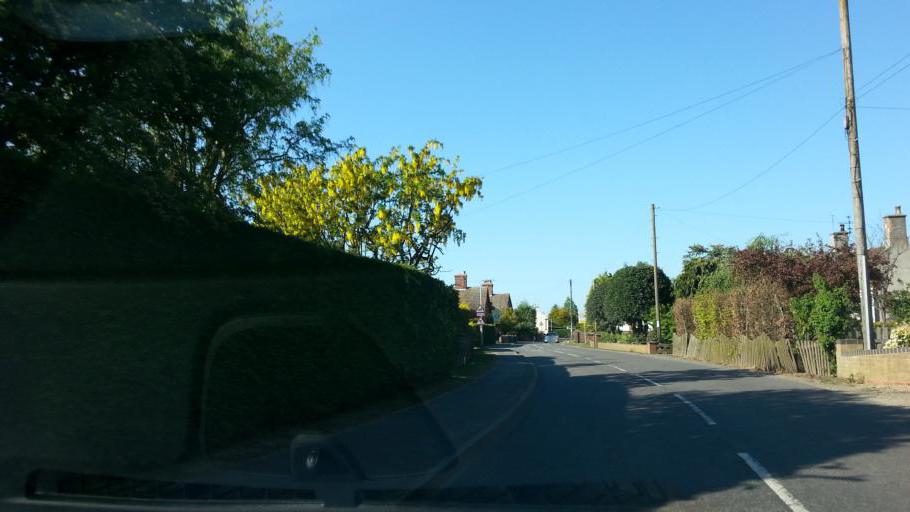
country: GB
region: England
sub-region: Lincolnshire
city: Great Gonerby
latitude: 52.9816
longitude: -0.6742
